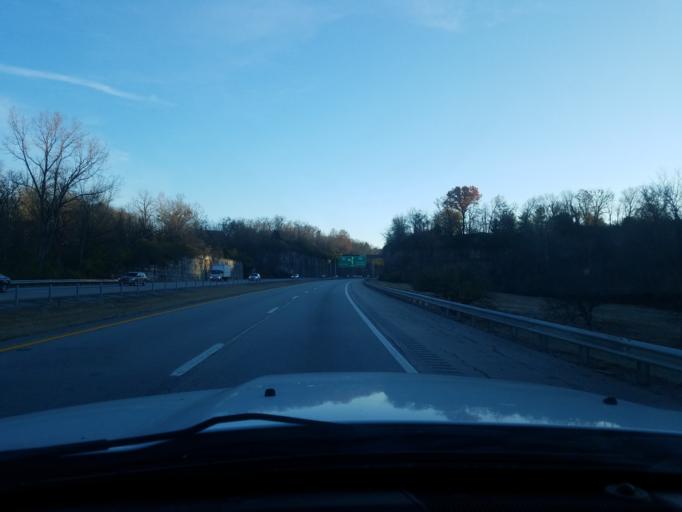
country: US
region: Kentucky
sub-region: Jefferson County
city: Indian Hills
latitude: 38.2921
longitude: -85.6690
